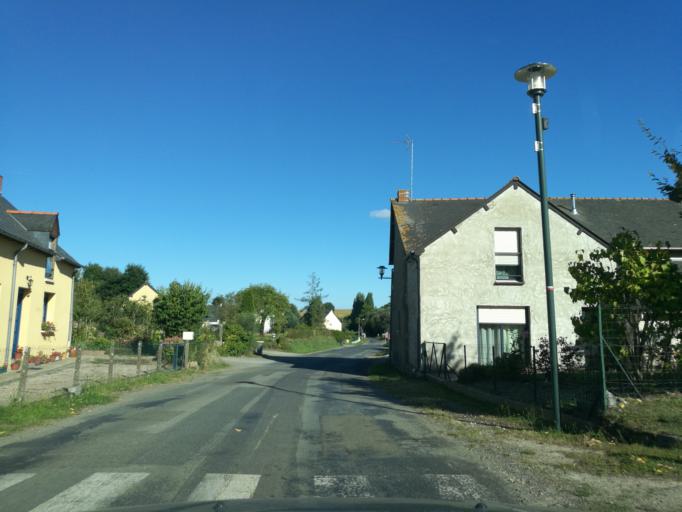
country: FR
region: Brittany
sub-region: Departement d'Ille-et-Vilaine
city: Montauban-de-Bretagne
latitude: 48.1731
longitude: -2.0275
